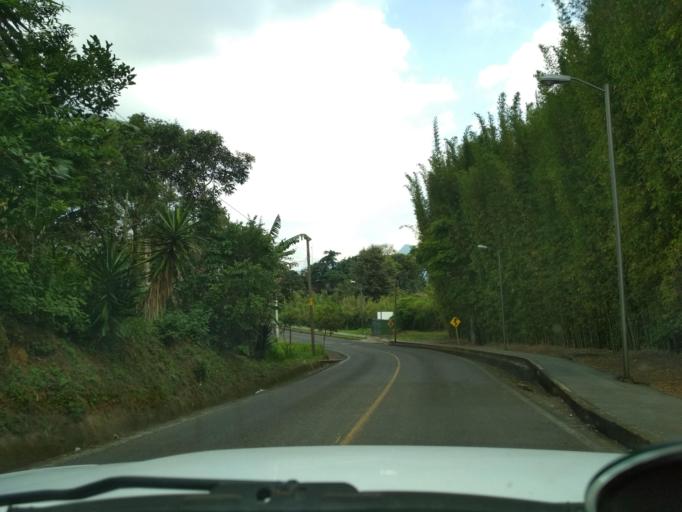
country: MX
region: Veracruz
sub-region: Ixtaczoquitlan
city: Buenavista
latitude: 18.9140
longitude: -97.0264
